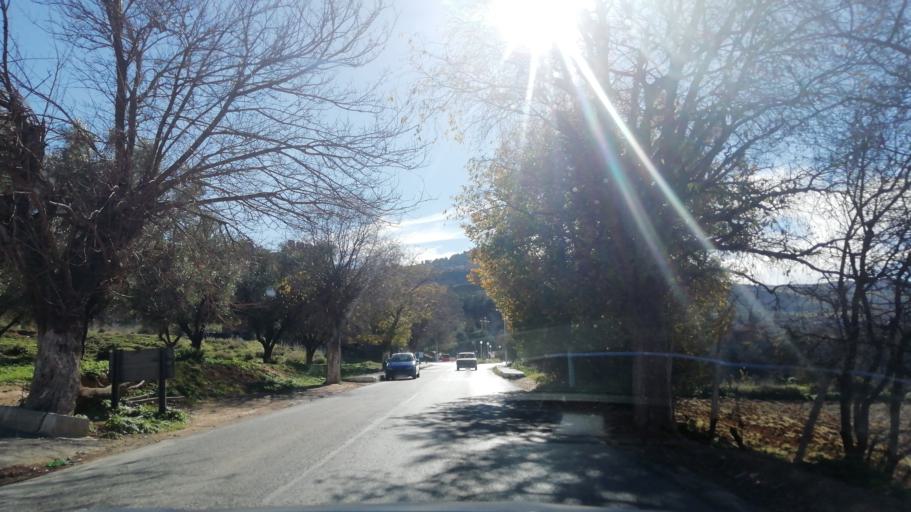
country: DZ
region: Tlemcen
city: Mansoura
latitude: 34.8663
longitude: -1.3332
